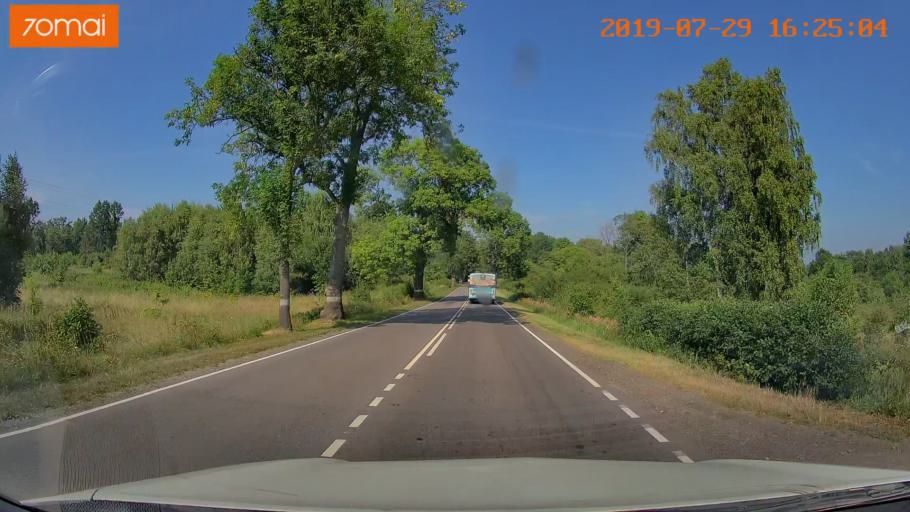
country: RU
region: Kaliningrad
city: Primorsk
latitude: 54.7200
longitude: 19.9628
